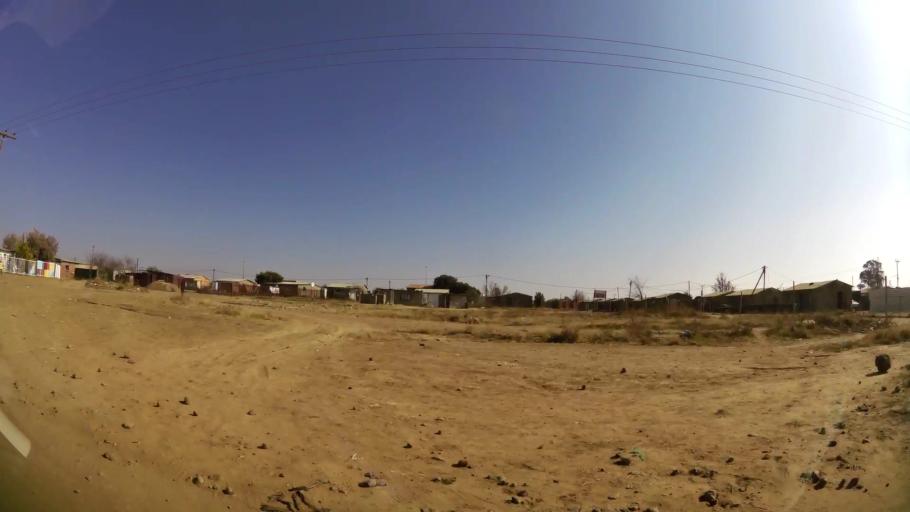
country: ZA
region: Orange Free State
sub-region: Mangaung Metropolitan Municipality
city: Bloemfontein
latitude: -29.1821
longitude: 26.2859
